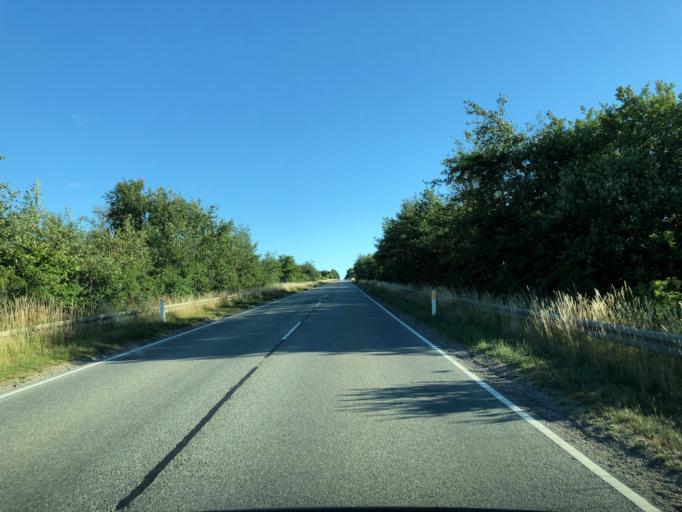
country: DK
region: Central Jutland
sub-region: Arhus Kommune
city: Framlev
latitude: 56.1246
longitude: 9.9925
